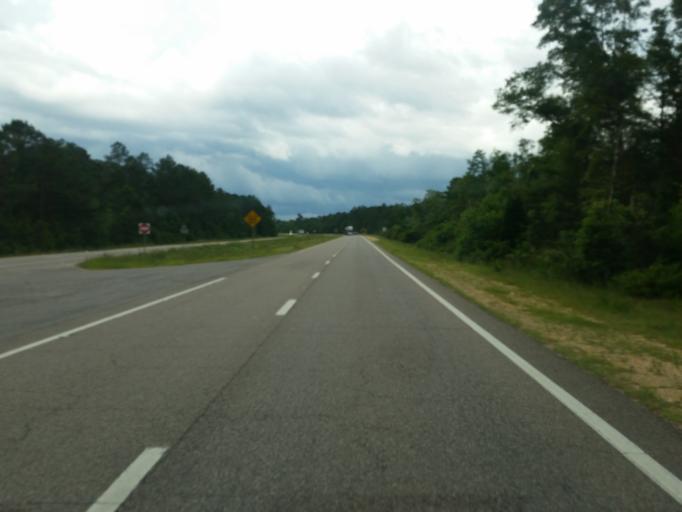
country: US
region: Mississippi
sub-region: George County
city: Lucedale
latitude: 30.8694
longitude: -88.4267
